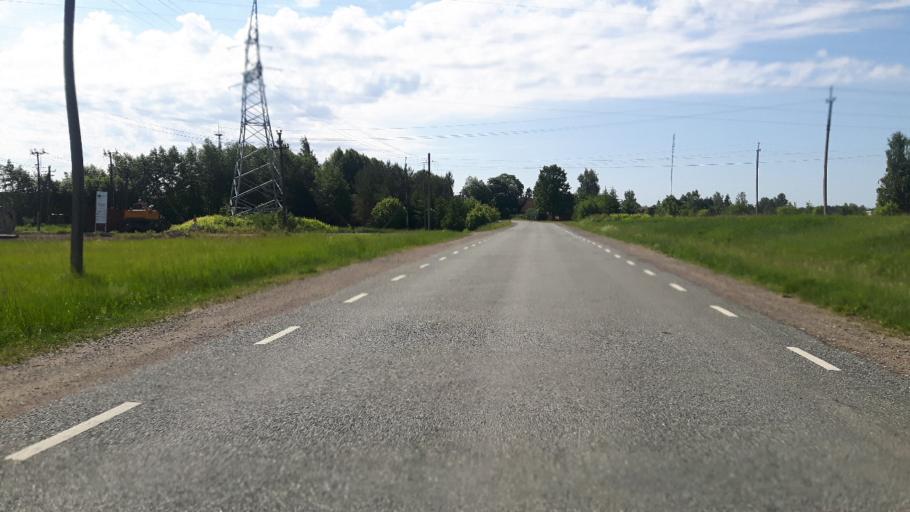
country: EE
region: Paernumaa
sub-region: Vaendra vald (alev)
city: Vandra
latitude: 58.6589
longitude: 25.0237
